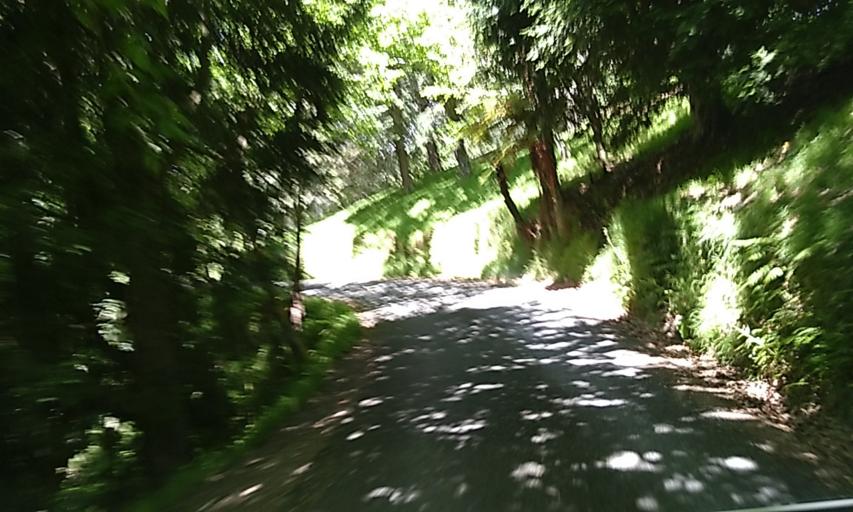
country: NZ
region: Bay of Plenty
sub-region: Tauranga City
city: Tauranga
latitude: -37.8144
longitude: 176.0420
